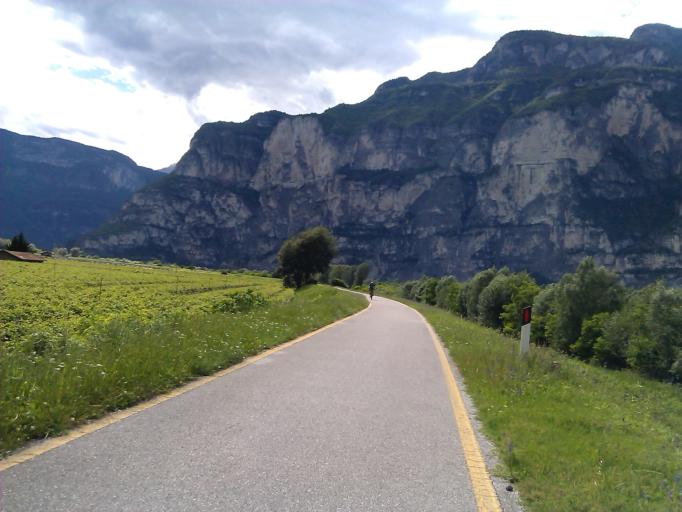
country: IT
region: Trentino-Alto Adige
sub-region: Provincia di Trento
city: Rovere della Luna
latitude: 46.2262
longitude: 11.1622
